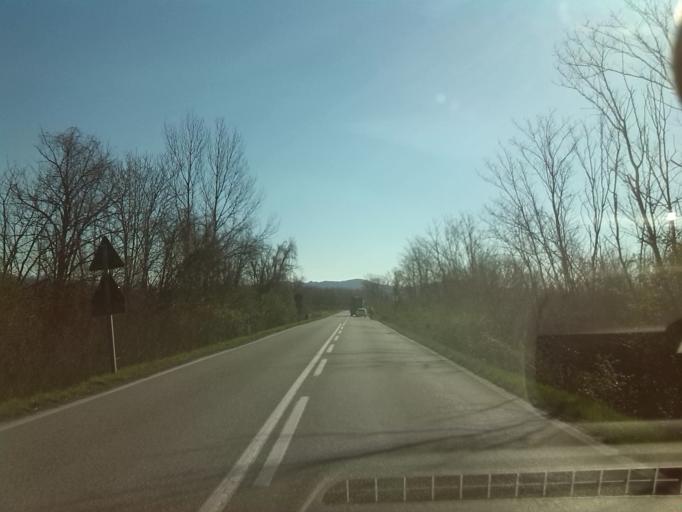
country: IT
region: Friuli Venezia Giulia
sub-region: Provincia di Udine
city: Moimacco
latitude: 46.0869
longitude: 13.3512
